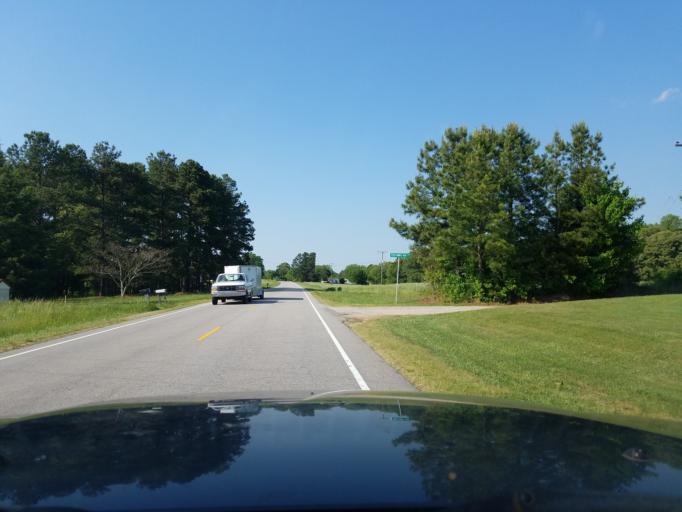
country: US
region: North Carolina
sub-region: Vance County
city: Henderson
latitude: 36.3742
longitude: -78.3710
